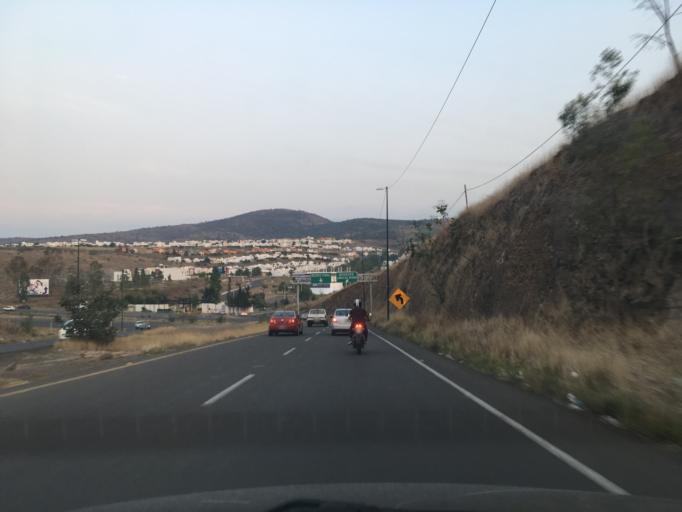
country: MX
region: Michoacan
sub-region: Morelia
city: La Aldea
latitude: 19.7310
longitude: -101.1067
